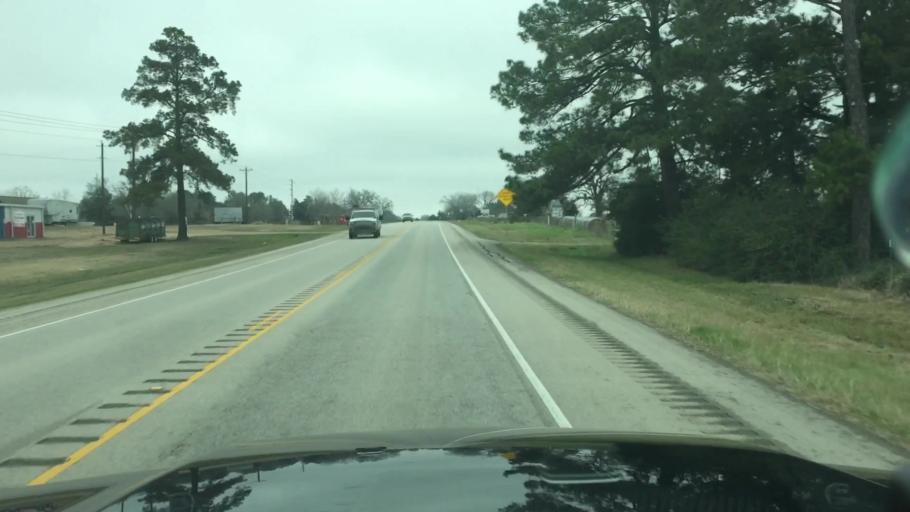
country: US
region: Texas
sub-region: Lee County
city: Giddings
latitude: 30.0518
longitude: -96.9142
